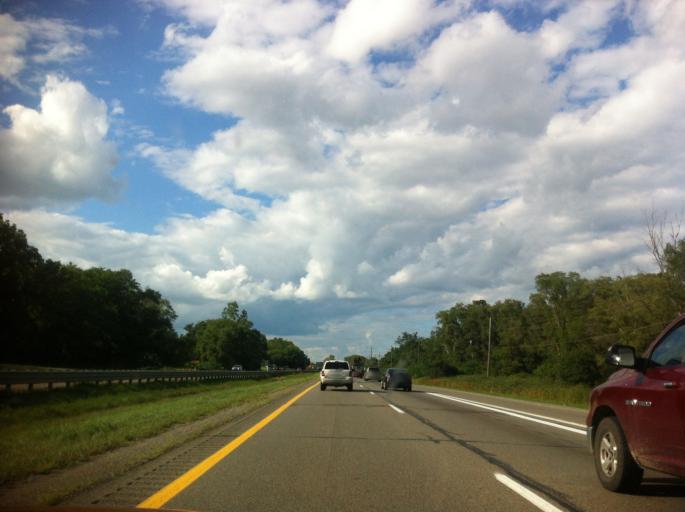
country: US
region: Michigan
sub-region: Livingston County
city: Whitmore Lake
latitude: 42.3970
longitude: -83.7634
